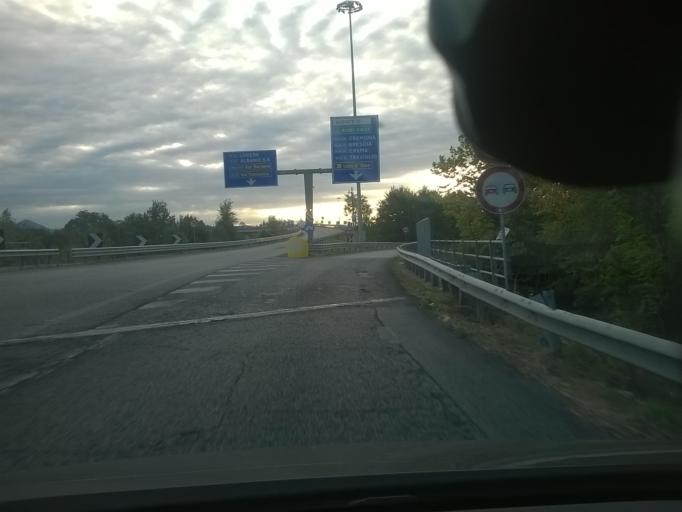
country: IT
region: Lombardy
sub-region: Provincia di Bergamo
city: Grassobbio
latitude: 45.6678
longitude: 9.7363
